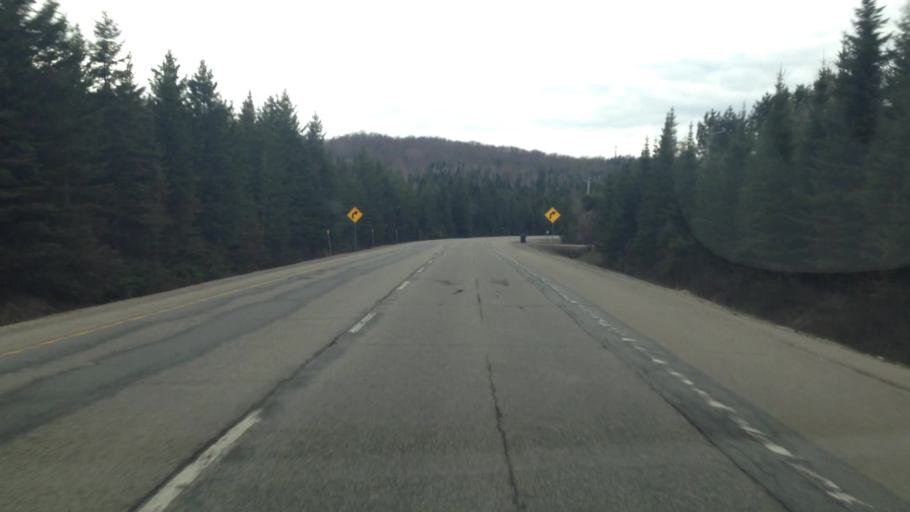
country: CA
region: Quebec
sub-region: Laurentides
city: Sainte-Agathe-des-Monts
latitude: 46.1110
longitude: -74.4219
